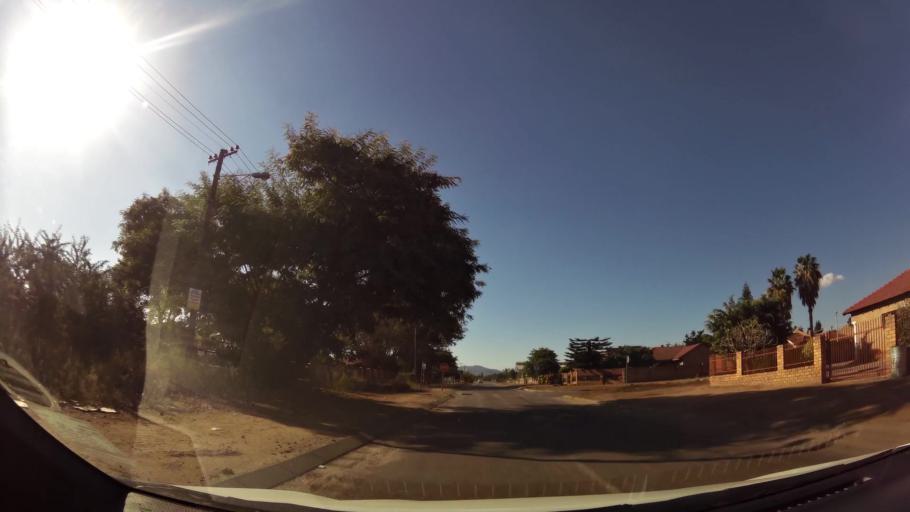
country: ZA
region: Limpopo
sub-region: Waterberg District Municipality
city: Mokopane
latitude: -24.1794
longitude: 28.9988
